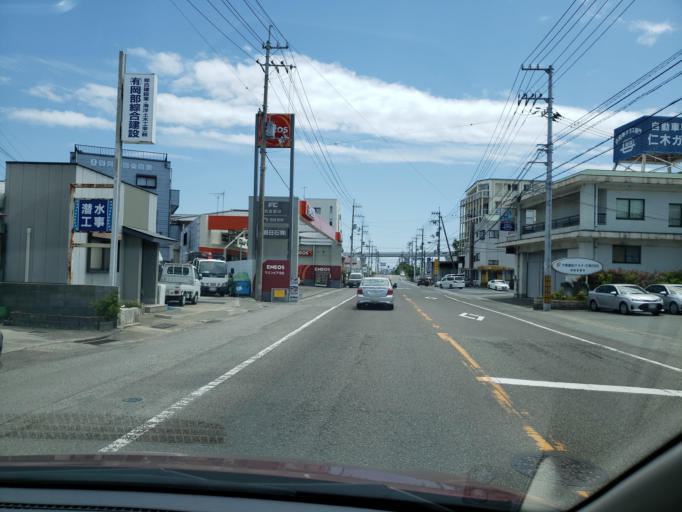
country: JP
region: Tokushima
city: Tokushima-shi
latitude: 34.0591
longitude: 134.5830
